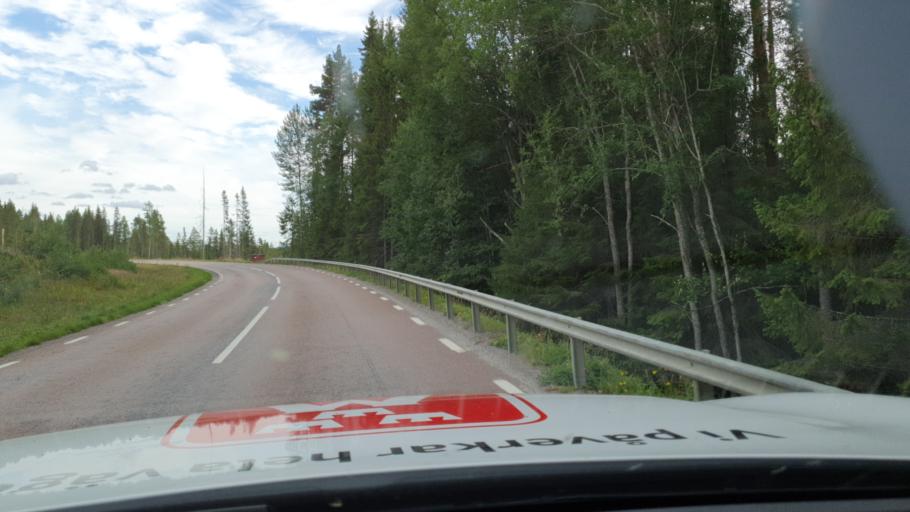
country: SE
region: Vaesternorrland
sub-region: Solleftea Kommun
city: As
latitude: 63.5739
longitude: 16.4057
